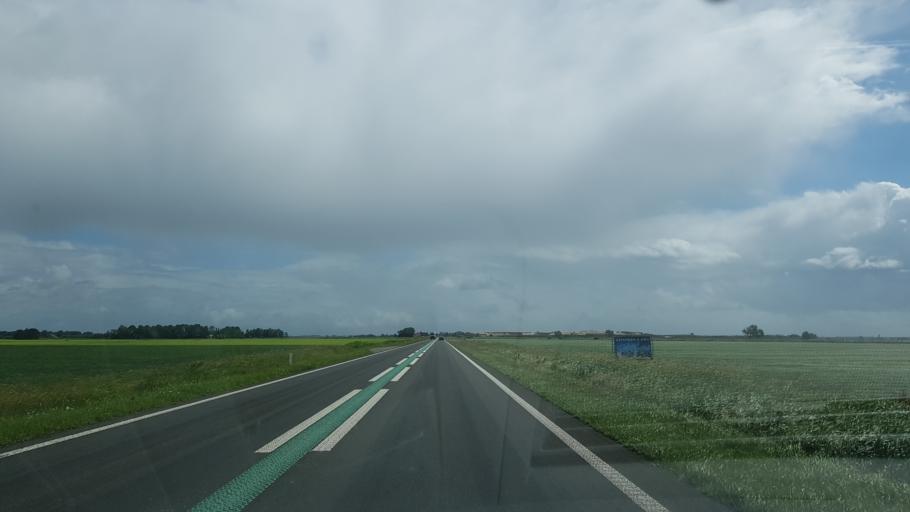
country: NL
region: Friesland
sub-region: Gemeente Ferwerderadiel
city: Burdaard
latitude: 53.2766
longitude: 5.8937
